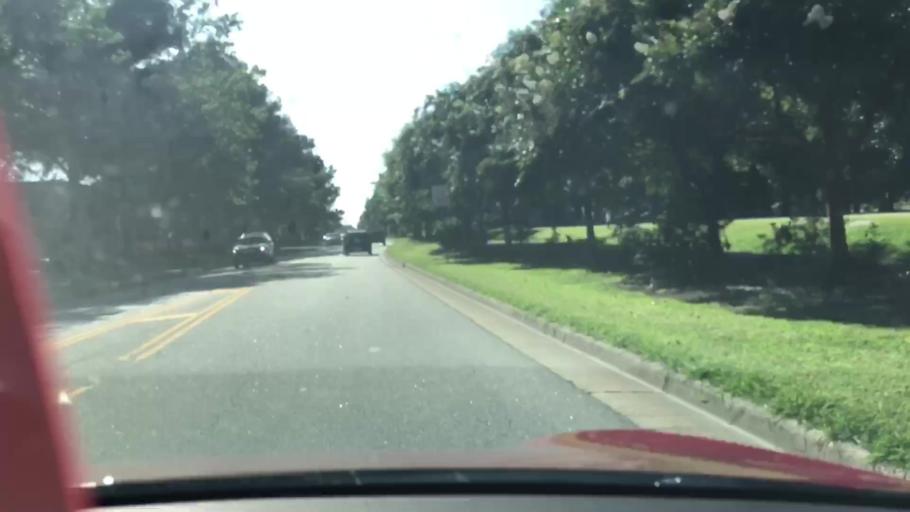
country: US
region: Virginia
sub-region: City of Virginia Beach
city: Virginia Beach
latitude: 36.8378
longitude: -75.9916
